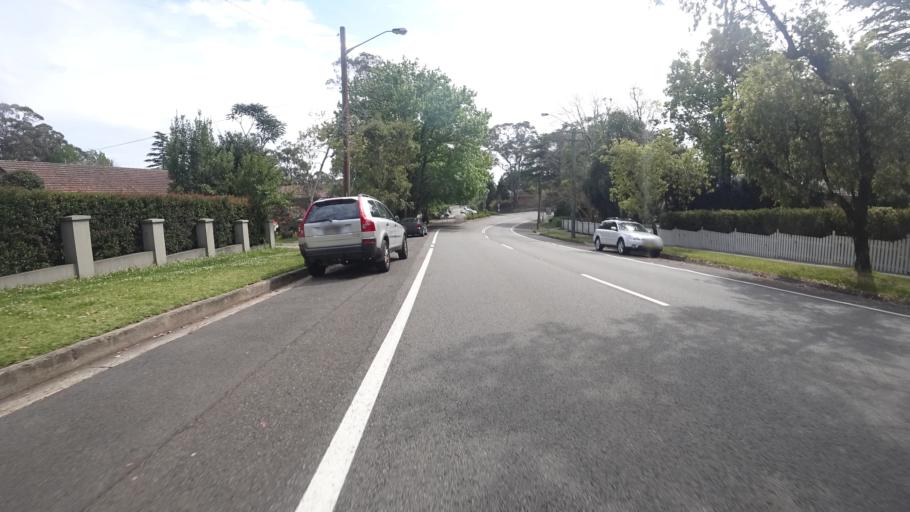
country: AU
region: New South Wales
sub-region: City of Sydney
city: North Turramurra
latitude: -33.7231
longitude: 151.1397
